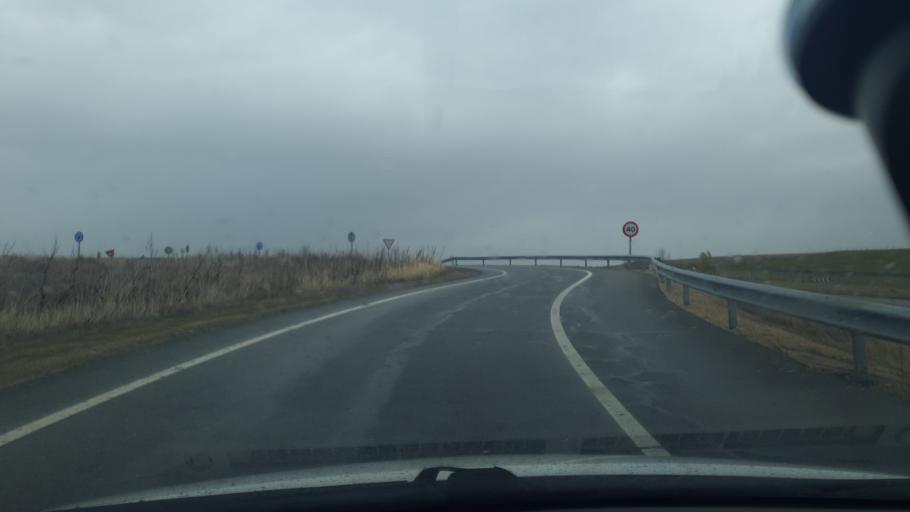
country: ES
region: Castille and Leon
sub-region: Provincia de Segovia
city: Carbonero el Mayor
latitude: 41.1116
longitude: -4.2531
